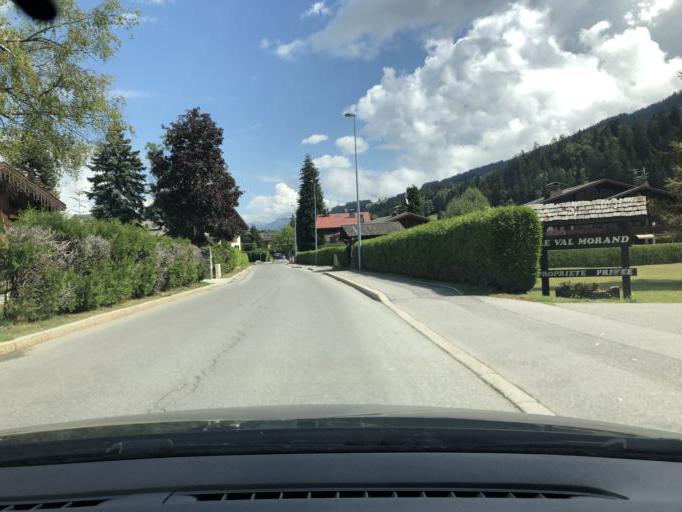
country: FR
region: Rhone-Alpes
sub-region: Departement de la Haute-Savoie
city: Megeve
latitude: 45.8646
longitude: 6.6227
